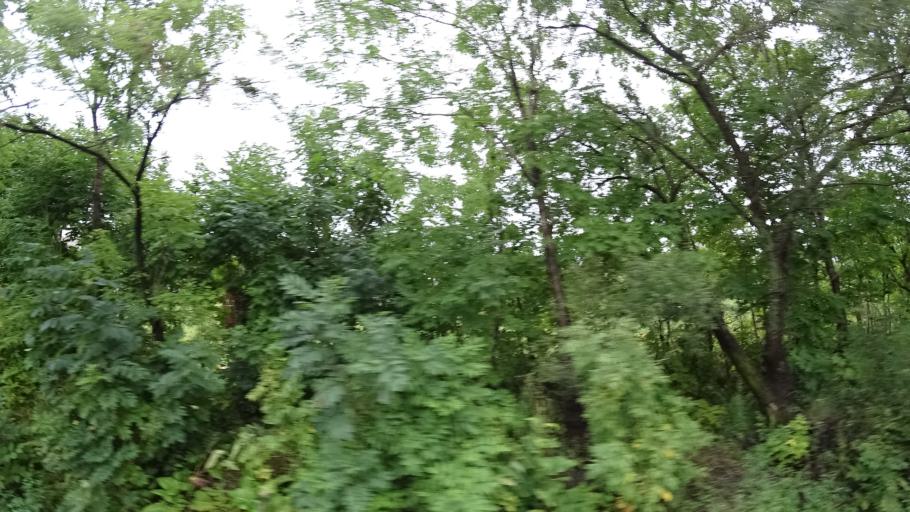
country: RU
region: Primorskiy
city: Monastyrishche
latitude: 44.2062
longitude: 132.4355
